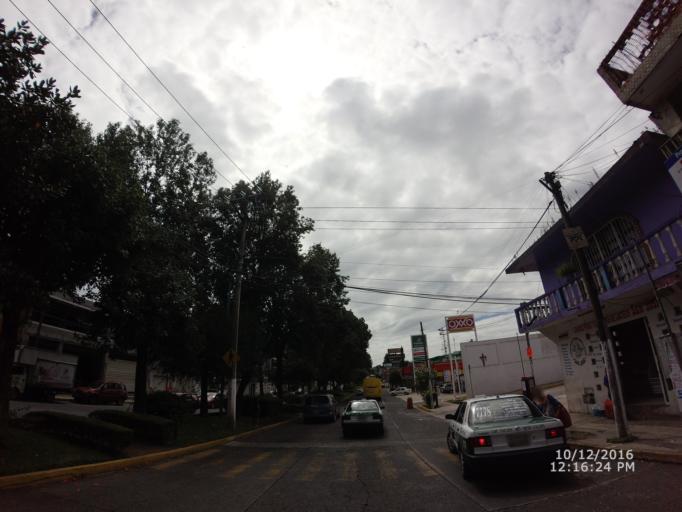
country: MX
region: Veracruz
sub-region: Xalapa
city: Xalapa de Enriquez
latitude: 19.5456
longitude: -96.9281
